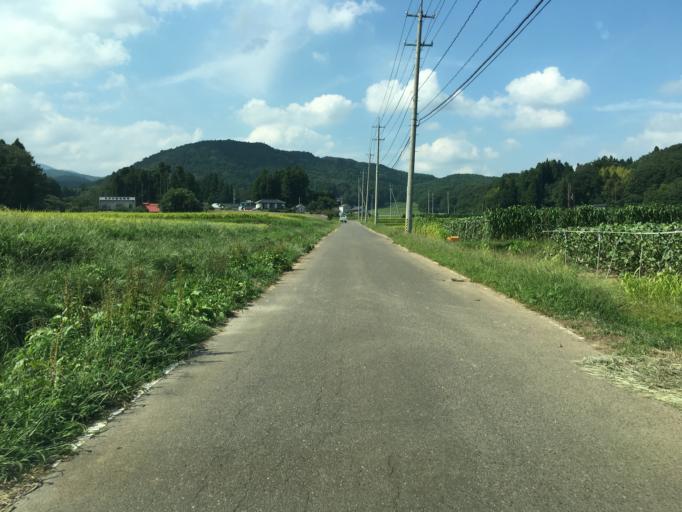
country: JP
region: Fukushima
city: Nihommatsu
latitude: 37.5937
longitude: 140.3863
